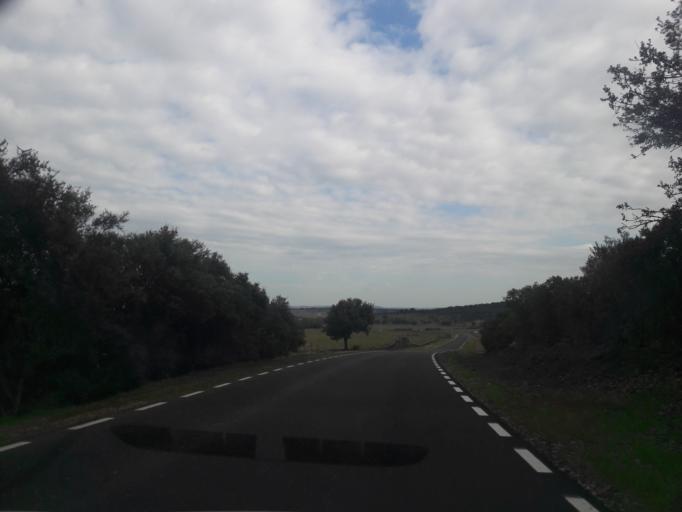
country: ES
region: Castille and Leon
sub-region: Provincia de Salamanca
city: Pastores
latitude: 40.5263
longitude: -6.5252
